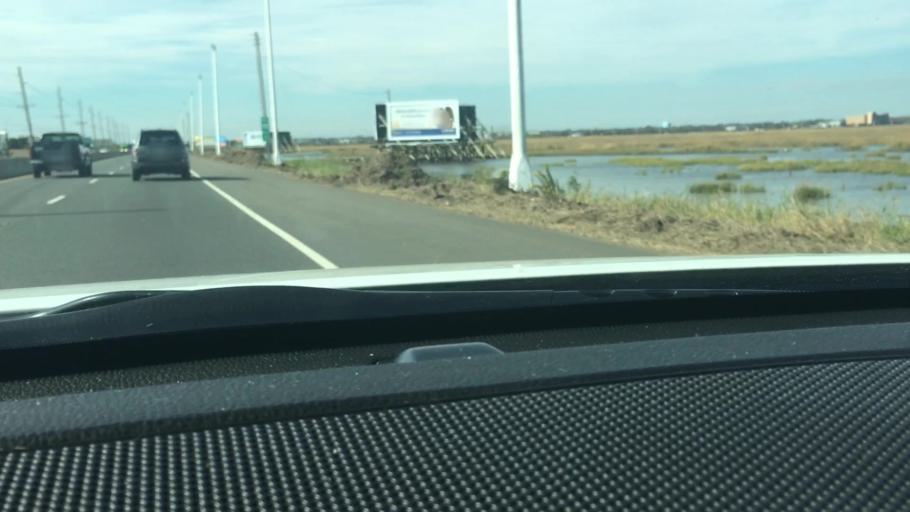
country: US
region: New Jersey
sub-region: Atlantic County
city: Absecon
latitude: 39.3888
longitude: -74.4792
